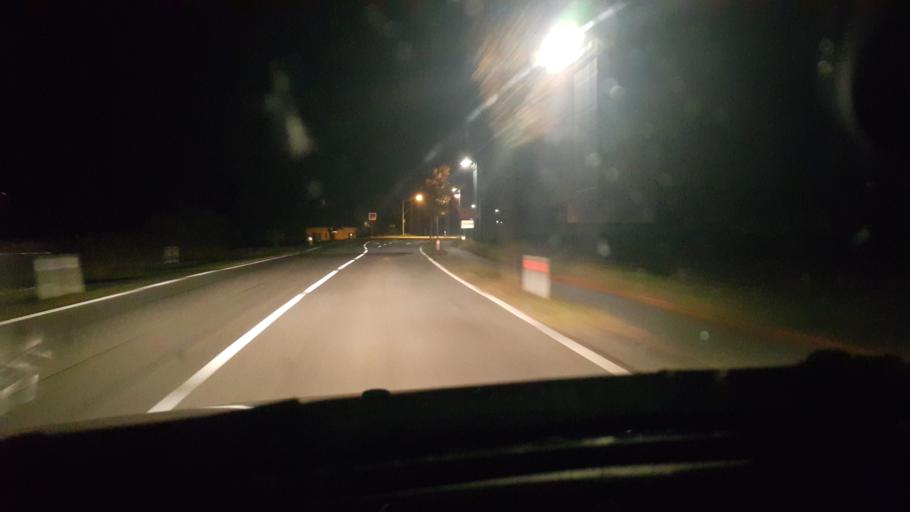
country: AT
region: Styria
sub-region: Politischer Bezirk Deutschlandsberg
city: Sankt Martin im Sulmtal
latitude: 46.7339
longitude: 15.3074
